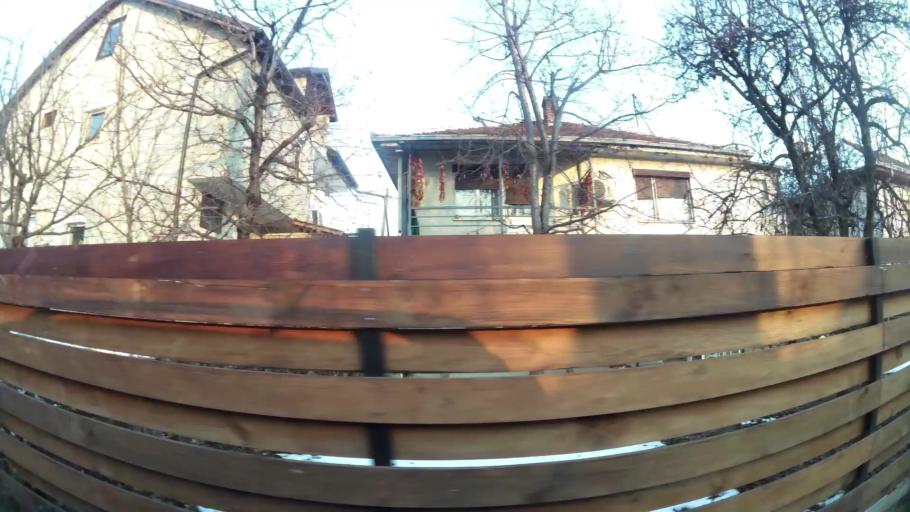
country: MK
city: Creshevo
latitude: 42.0157
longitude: 21.5206
